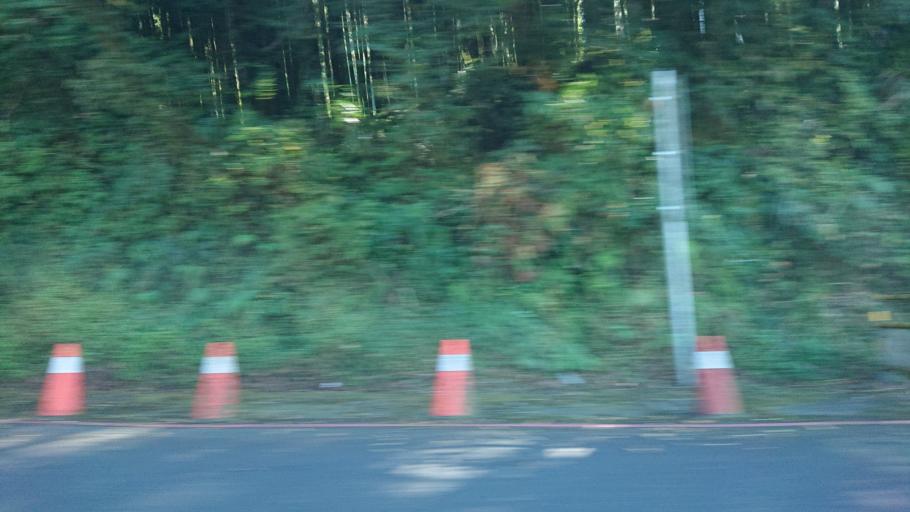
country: TW
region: Taiwan
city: Lugu
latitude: 23.5081
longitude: 120.8010
